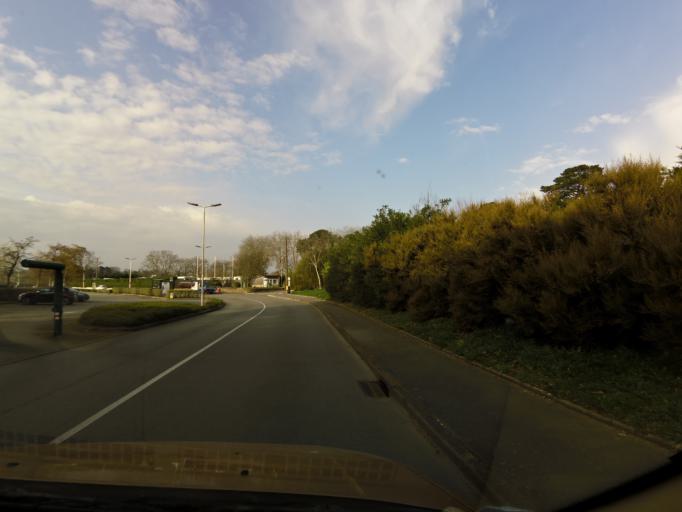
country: FR
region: Brittany
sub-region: Departement du Morbihan
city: Arradon
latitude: 47.6331
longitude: -2.7788
